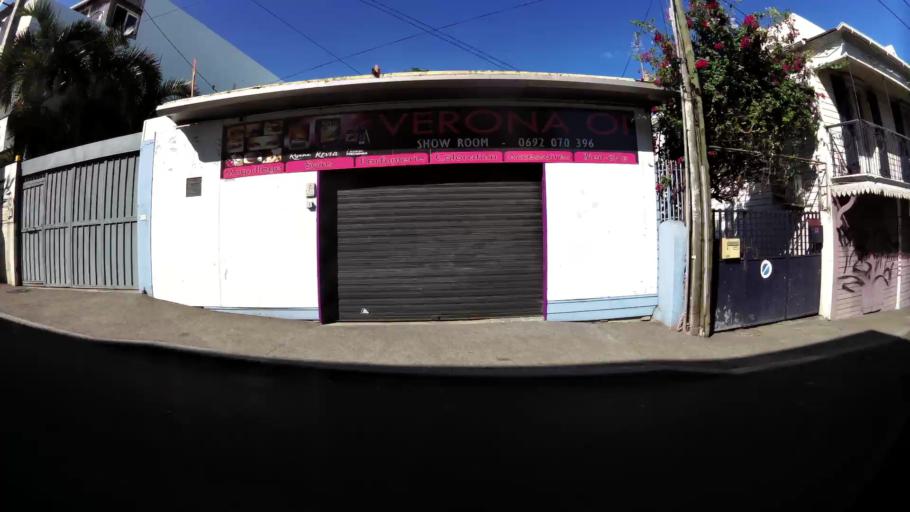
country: RE
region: Reunion
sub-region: Reunion
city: Saint-Pierre
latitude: -21.3409
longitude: 55.4787
